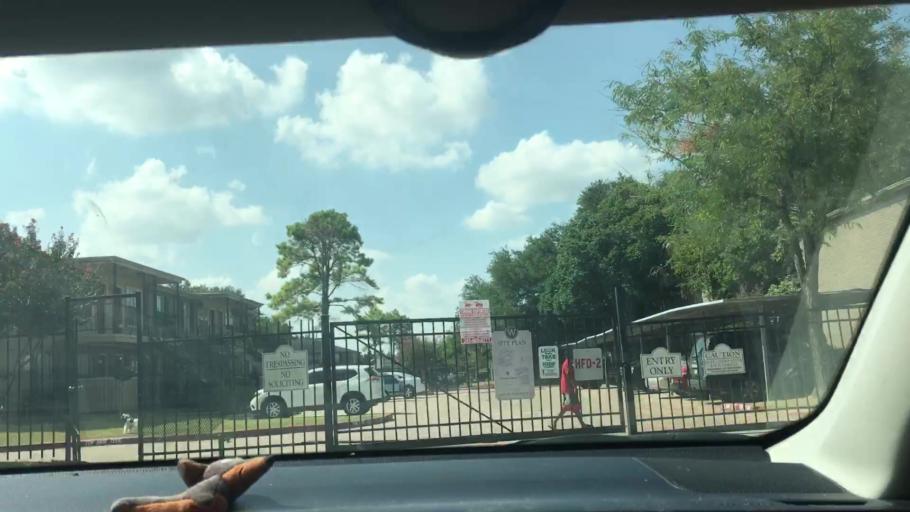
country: US
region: Texas
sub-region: Harris County
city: Bunker Hill Village
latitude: 29.7274
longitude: -95.5695
